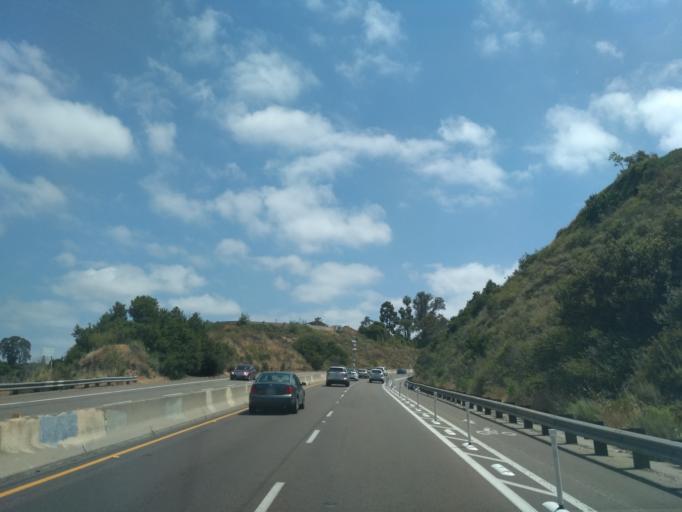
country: US
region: California
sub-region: San Diego County
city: La Jolla
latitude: 32.8144
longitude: -117.1940
